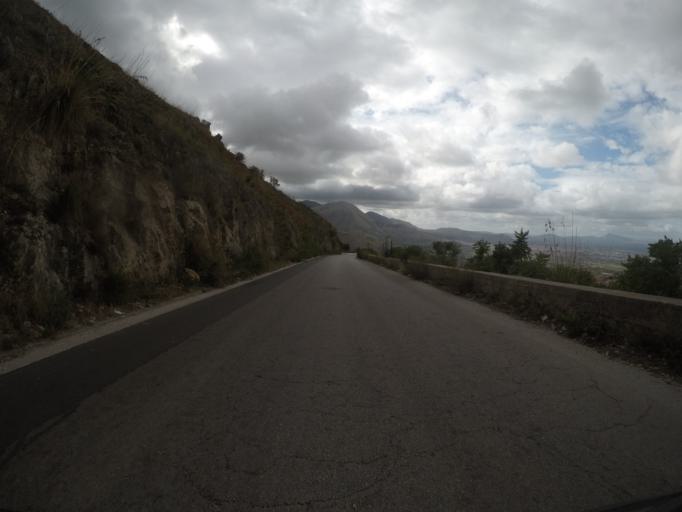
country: IT
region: Sicily
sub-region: Palermo
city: Montelepre
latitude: 38.0969
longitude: 13.1672
